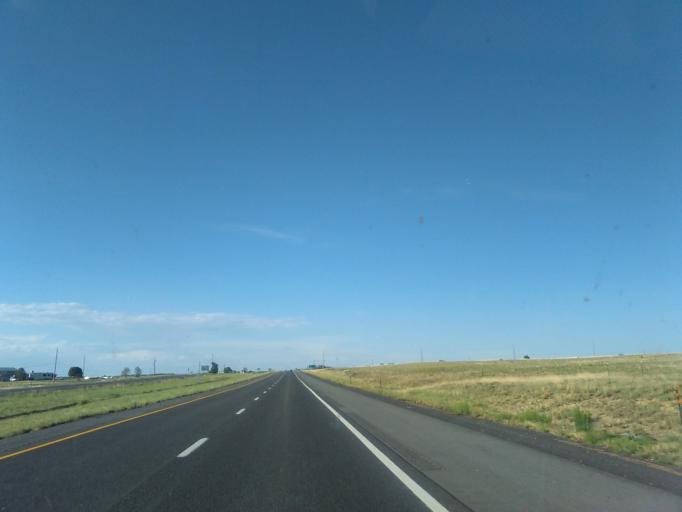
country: US
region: New Mexico
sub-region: San Miguel County
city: Las Vegas
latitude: 35.6351
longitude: -105.1994
